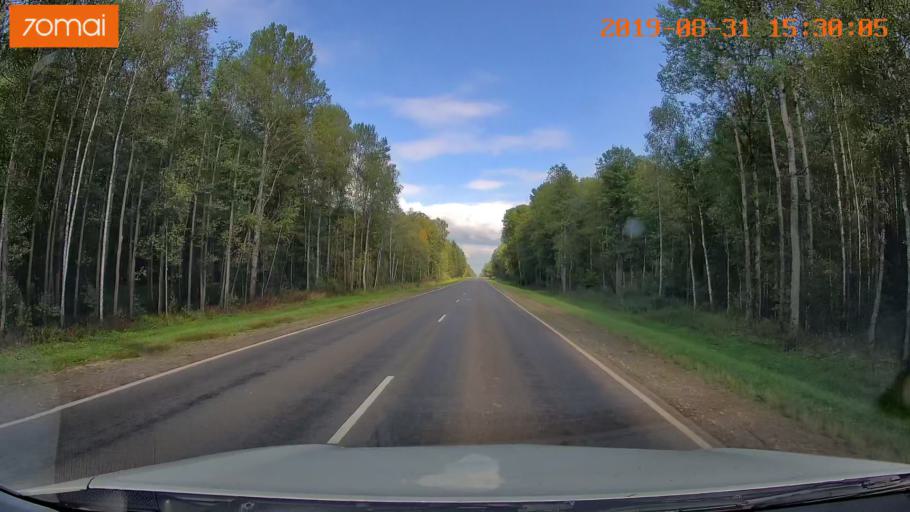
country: RU
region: Kaluga
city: Baryatino
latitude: 54.5733
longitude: 34.6214
